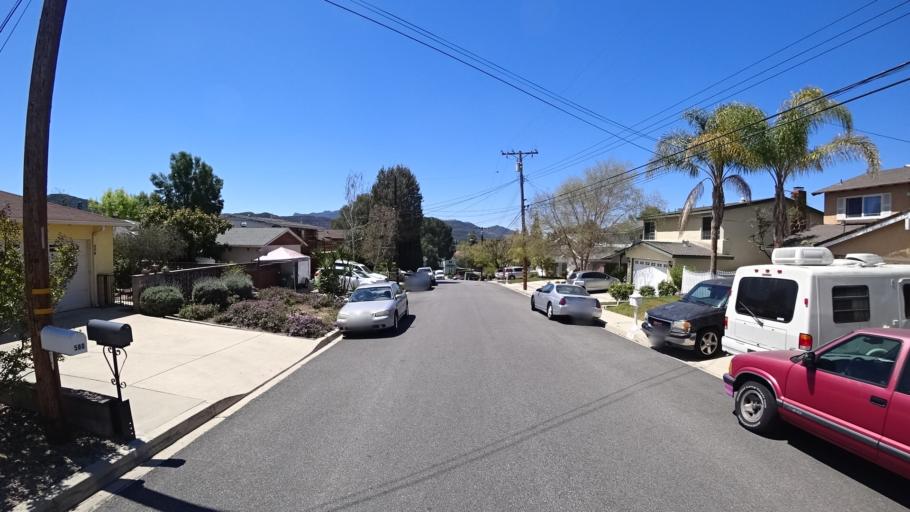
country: US
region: California
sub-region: Ventura County
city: Thousand Oaks
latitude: 34.1840
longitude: -118.8668
